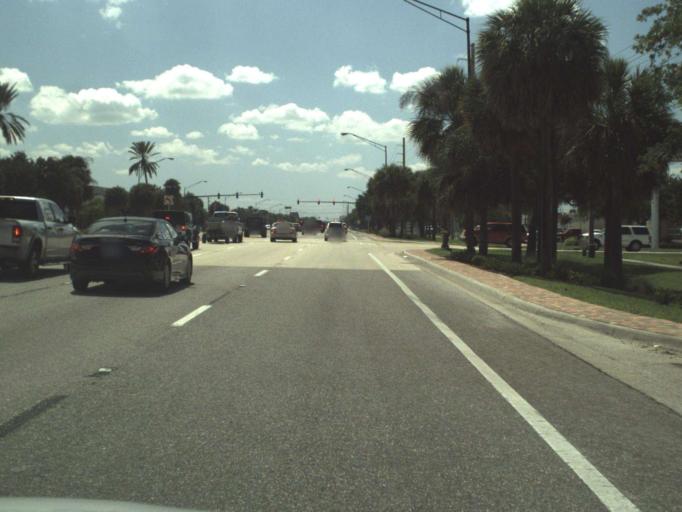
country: US
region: Florida
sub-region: Brevard County
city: Rockledge
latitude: 28.3573
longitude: -80.6856
